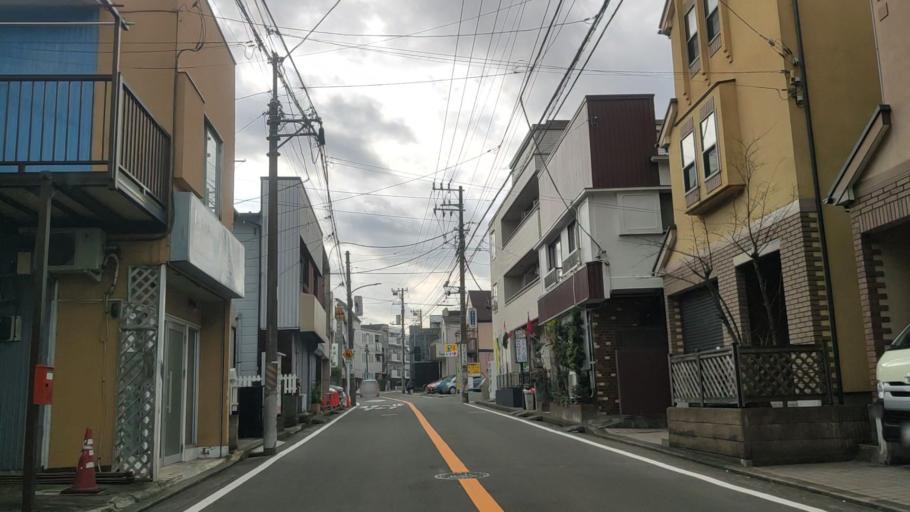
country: JP
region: Kanagawa
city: Yokohama
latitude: 35.4850
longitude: 139.6228
